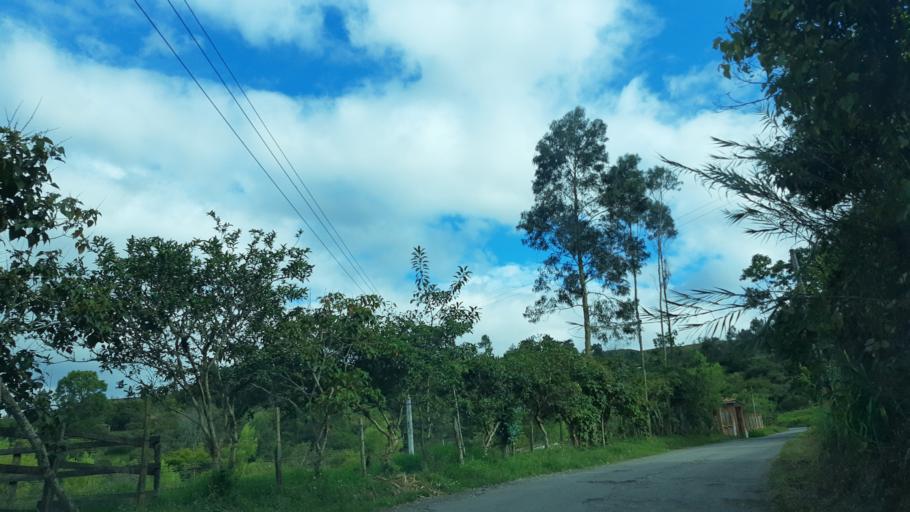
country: CO
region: Cundinamarca
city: Tenza
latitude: 5.0599
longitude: -73.4210
